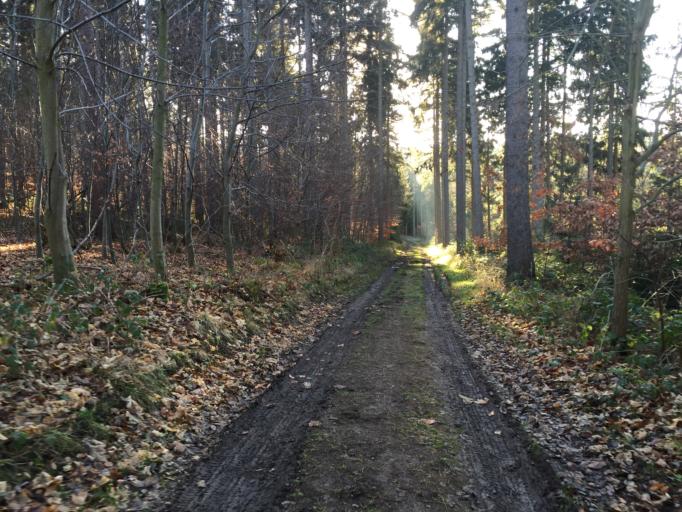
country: DE
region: Thuringia
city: Schmorda
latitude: 50.6596
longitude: 11.5904
